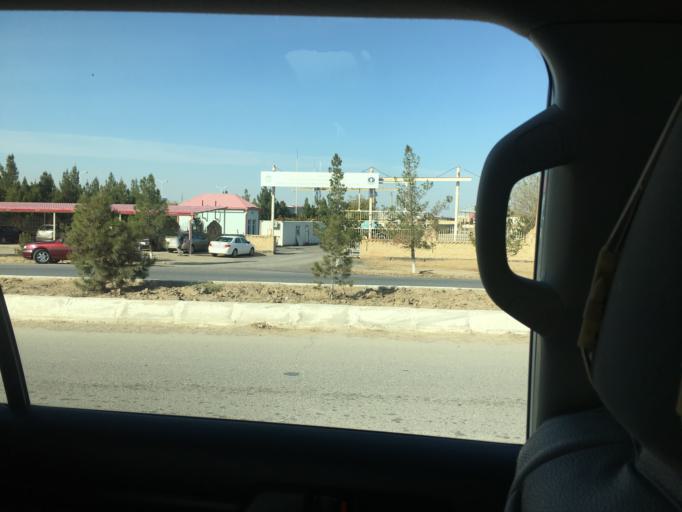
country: TM
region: Mary
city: Mary
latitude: 37.6030
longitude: 61.5833
